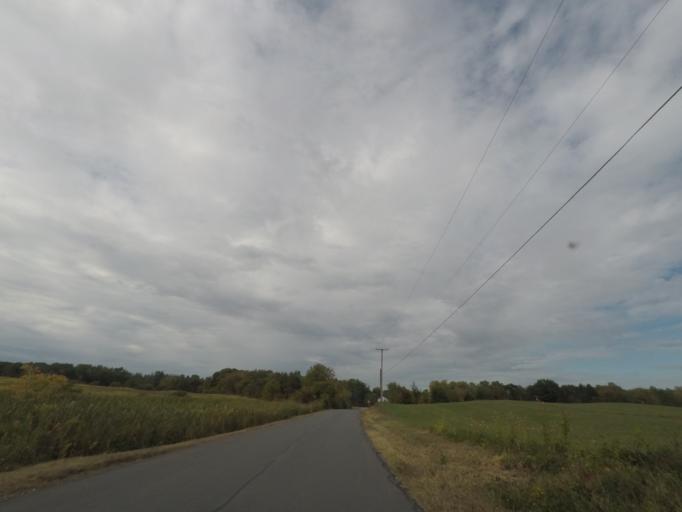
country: US
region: New York
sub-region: Rensselaer County
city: Nassau
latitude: 42.5322
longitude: -73.6439
